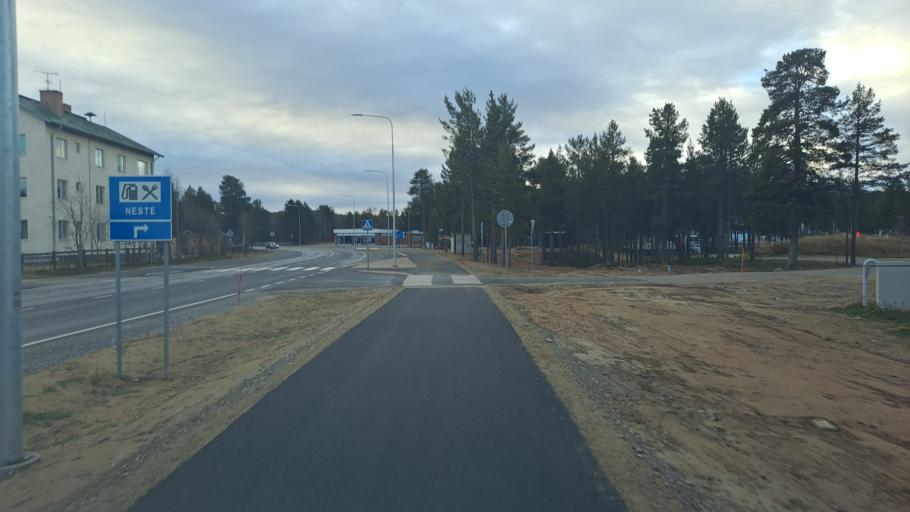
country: FI
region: Lapland
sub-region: Pohjois-Lappi
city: Inari
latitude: 68.9081
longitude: 27.0141
